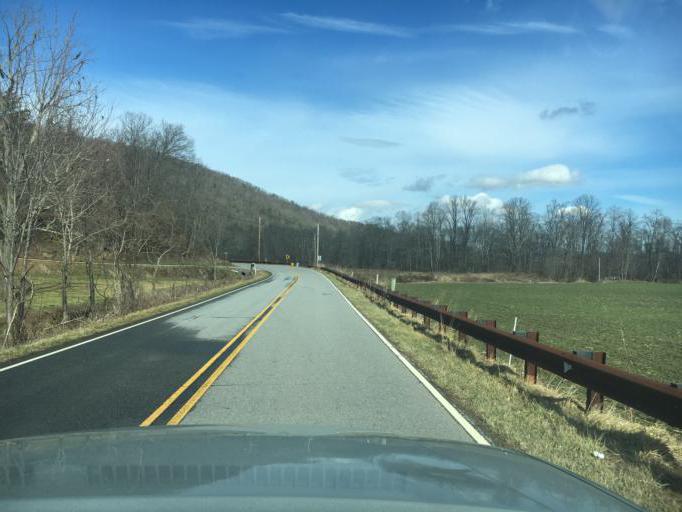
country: US
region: North Carolina
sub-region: Haywood County
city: Clyde
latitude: 35.4912
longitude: -82.8847
